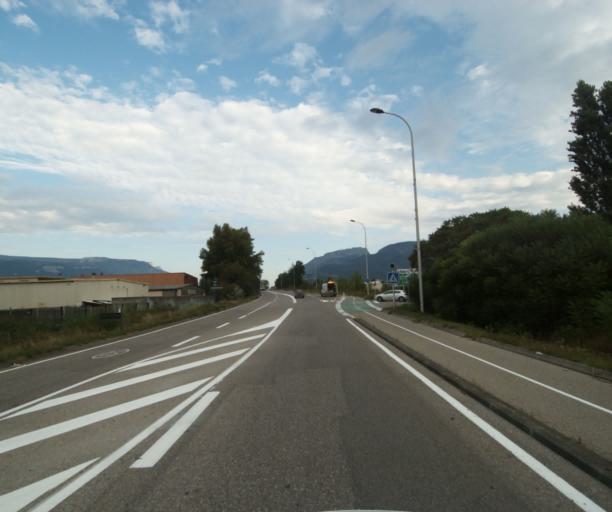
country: FR
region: Rhone-Alpes
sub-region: Departement de l'Isere
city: Saint-Martin-d'Heres
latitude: 45.1643
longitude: 5.7604
